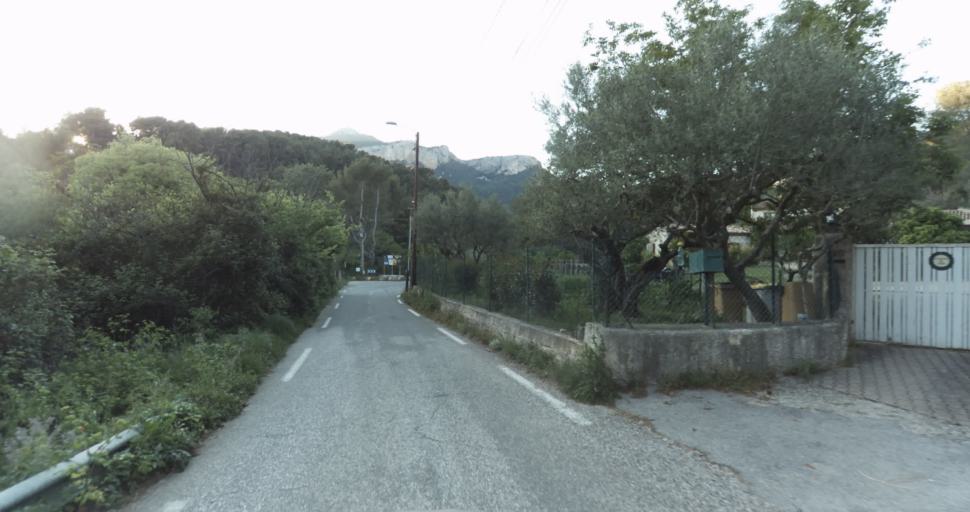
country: FR
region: Provence-Alpes-Cote d'Azur
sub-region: Departement du Var
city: Le Revest-les-Eaux
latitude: 43.1703
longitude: 5.9341
